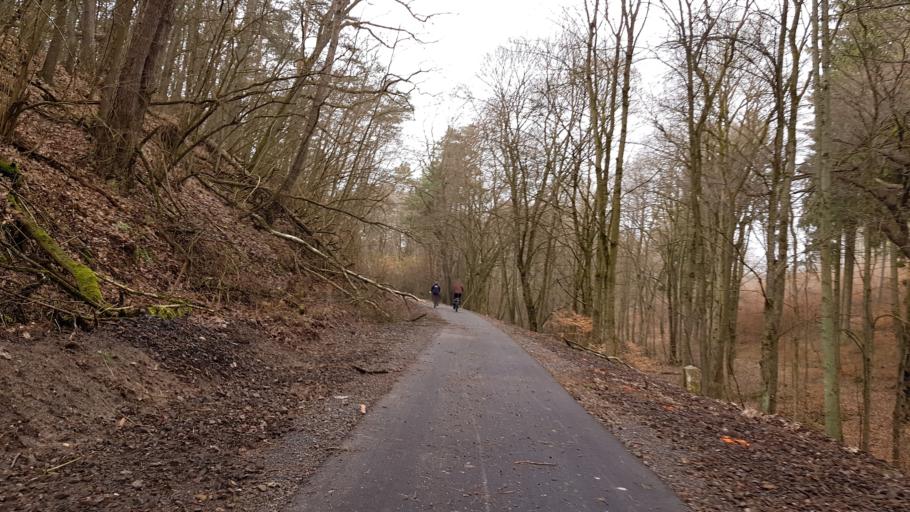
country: PL
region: West Pomeranian Voivodeship
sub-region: Powiat mysliborski
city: Barlinek
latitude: 53.0154
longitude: 15.2488
